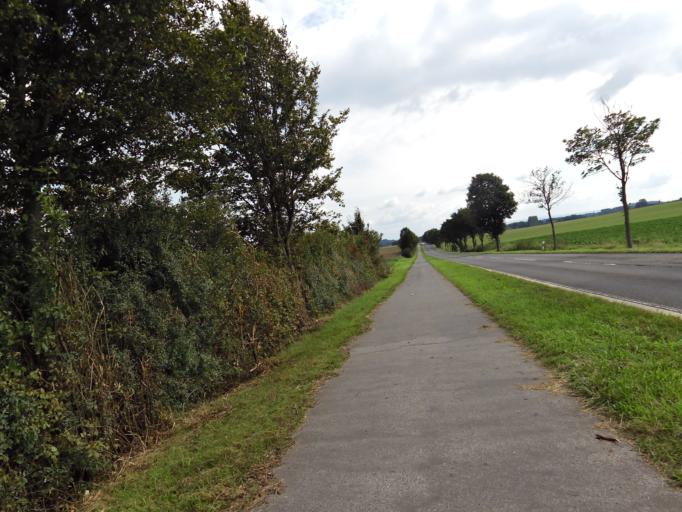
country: NL
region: Limburg
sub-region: Gemeente Kerkrade
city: Kerkrade
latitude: 50.8428
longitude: 6.0258
